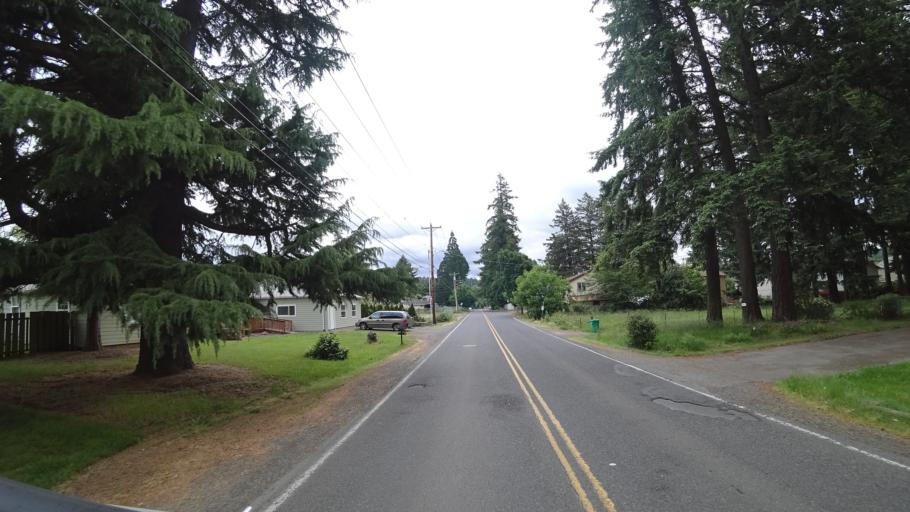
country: US
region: Oregon
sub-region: Clackamas County
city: Happy Valley
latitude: 45.4835
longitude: -122.5273
